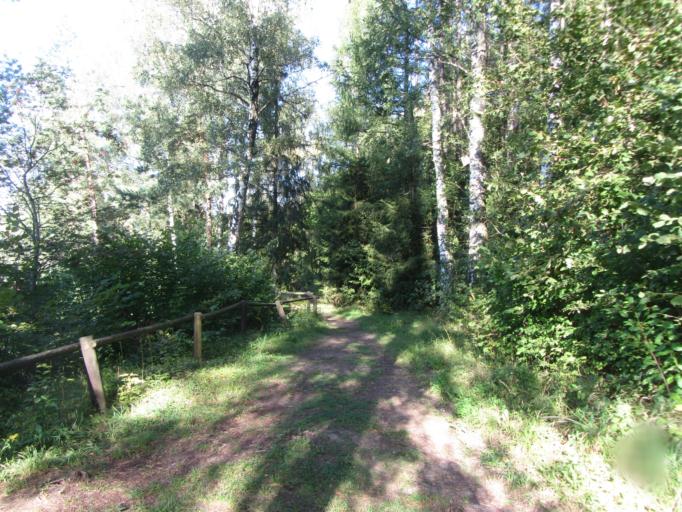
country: LT
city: Birstonas
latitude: 54.6051
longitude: 24.0037
